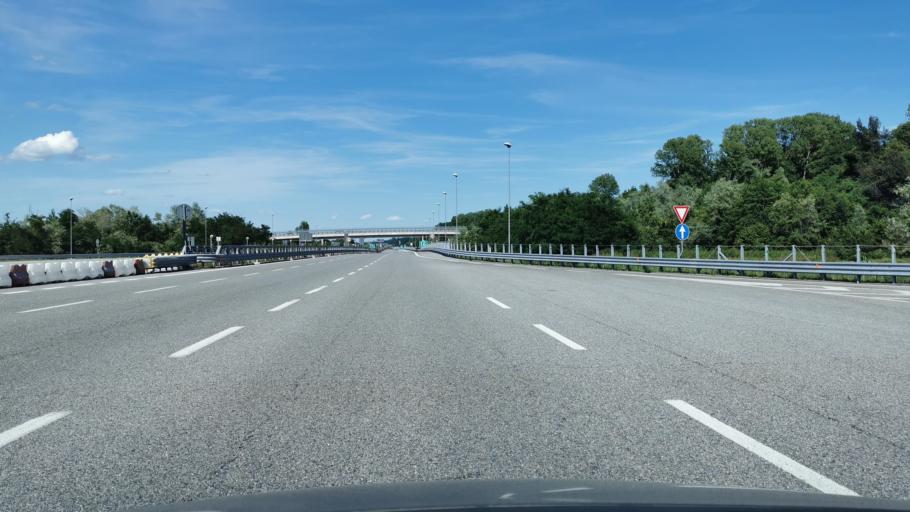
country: IT
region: Piedmont
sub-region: Provincia di Cuneo
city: Castelletto Stura
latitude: 44.4312
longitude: 7.6097
